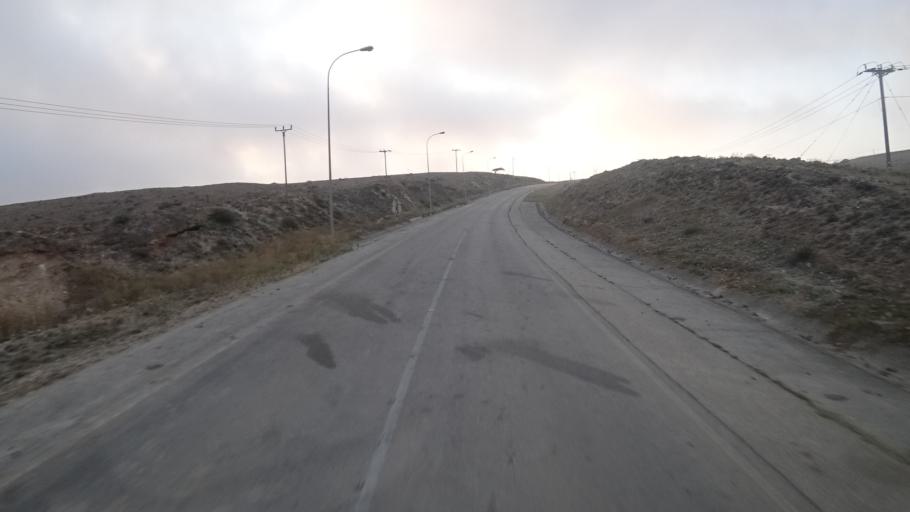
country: OM
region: Zufar
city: Salalah
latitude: 17.1207
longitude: 53.9317
